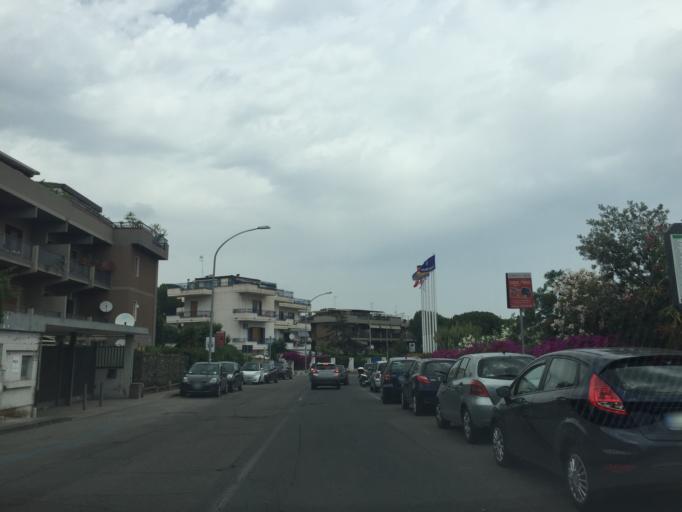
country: IT
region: Sicily
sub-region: Catania
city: Aci Castello
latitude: 37.5397
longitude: 15.1317
